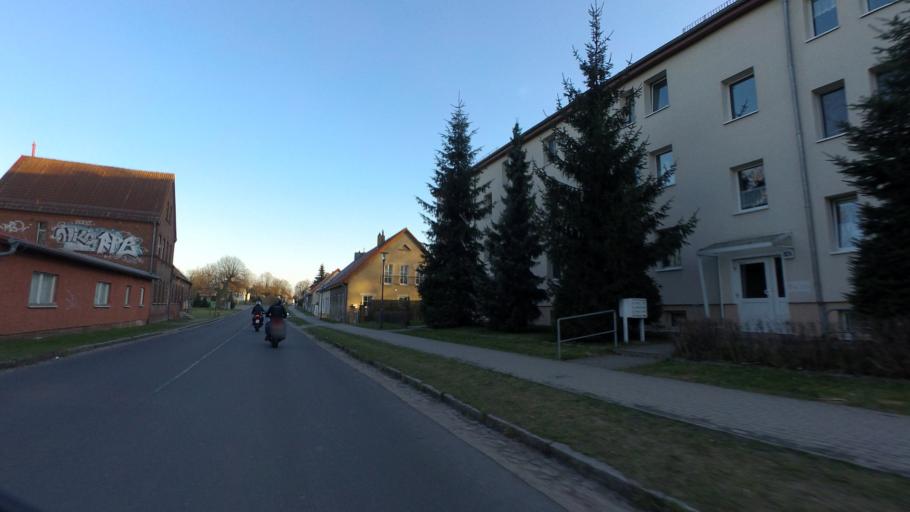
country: DE
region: Berlin
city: Hellersdorf
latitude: 52.5466
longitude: 13.6375
